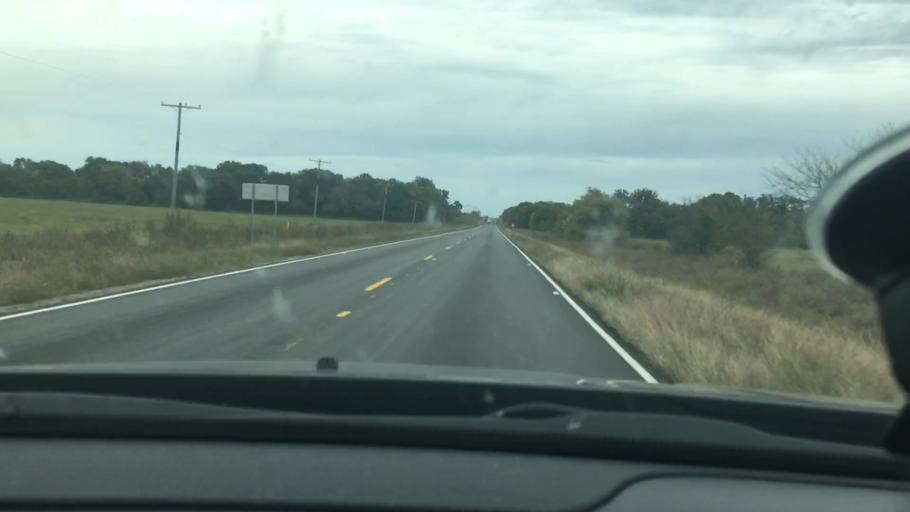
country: US
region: Oklahoma
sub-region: Coal County
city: Coalgate
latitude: 34.4017
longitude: -96.4245
